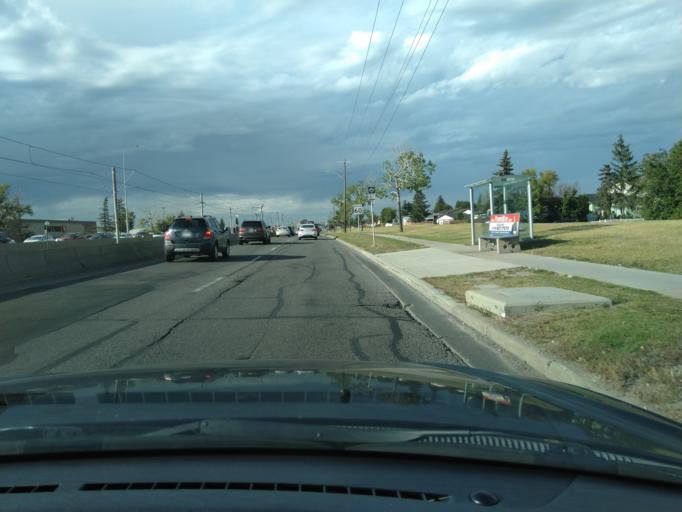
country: CA
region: Alberta
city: Calgary
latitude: 51.0819
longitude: -113.9815
